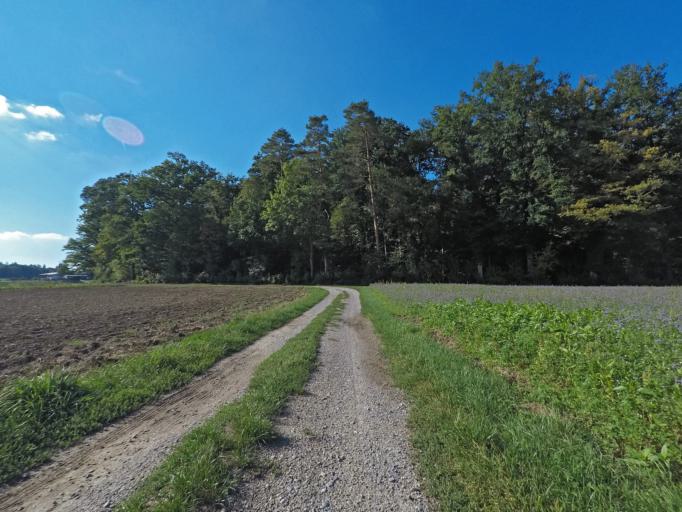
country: CH
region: Thurgau
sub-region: Frauenfeld District
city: Diessenhofen
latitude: 47.6521
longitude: 8.7425
